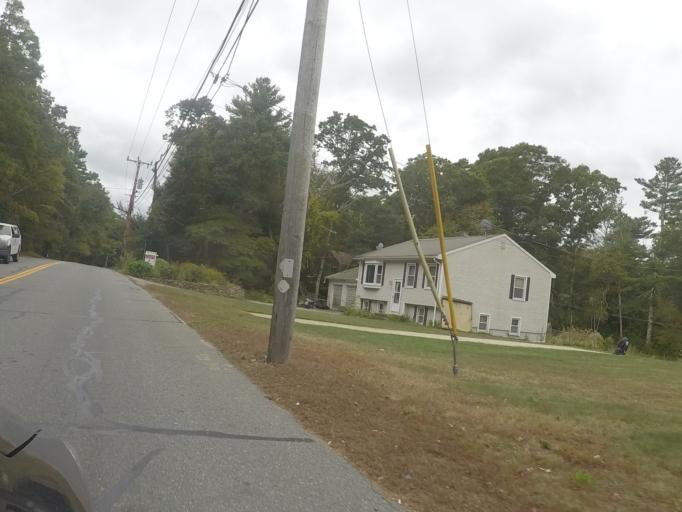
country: US
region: Massachusetts
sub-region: Bristol County
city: Smith Mills
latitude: 41.5825
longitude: -71.0027
